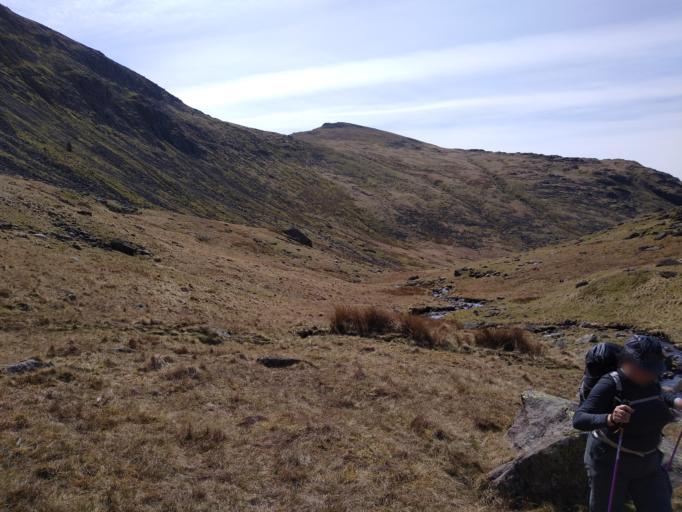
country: GB
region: England
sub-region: Cumbria
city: Ambleside
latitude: 54.3870
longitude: -3.1310
